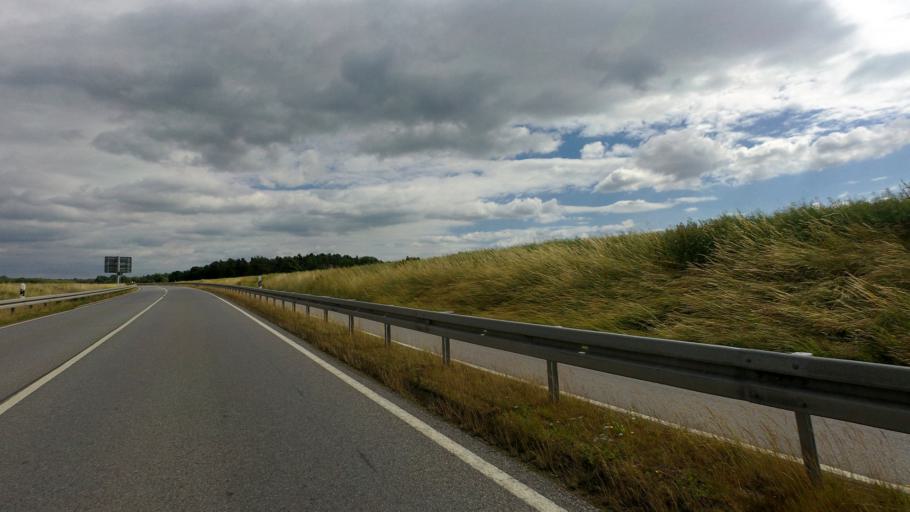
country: DE
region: Saxony
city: Nebelschutz
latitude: 51.2827
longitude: 14.1309
